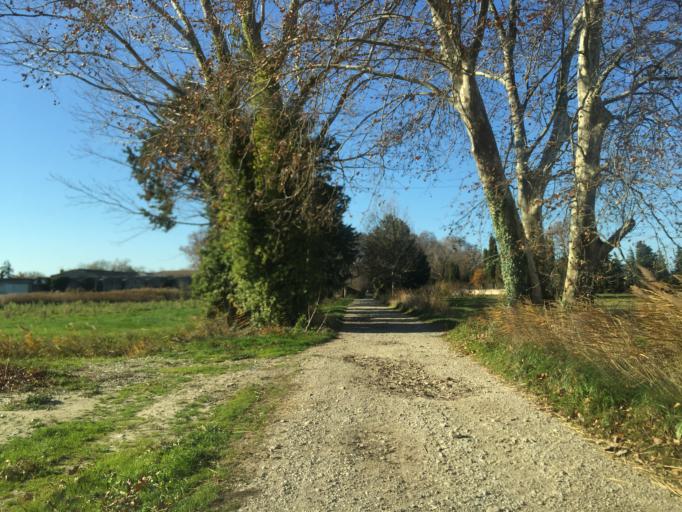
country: FR
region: Provence-Alpes-Cote d'Azur
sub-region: Departement du Vaucluse
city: Bedarrides
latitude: 44.0659
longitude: 4.9248
